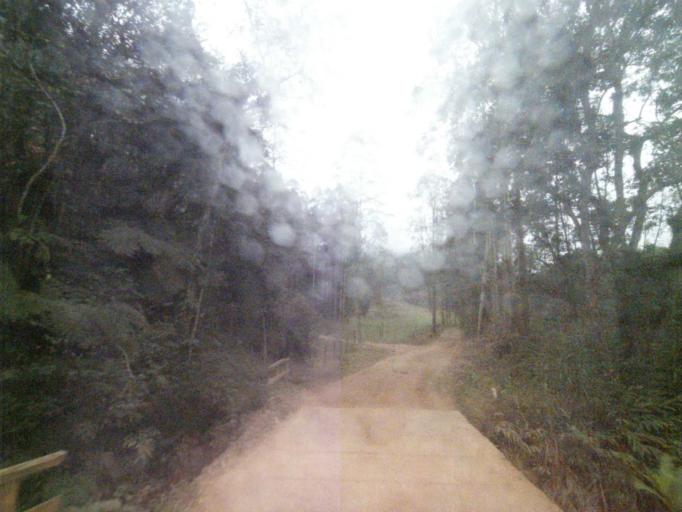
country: BR
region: Santa Catarina
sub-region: Anitapolis
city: Anitapolis
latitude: -27.8783
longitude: -49.1340
